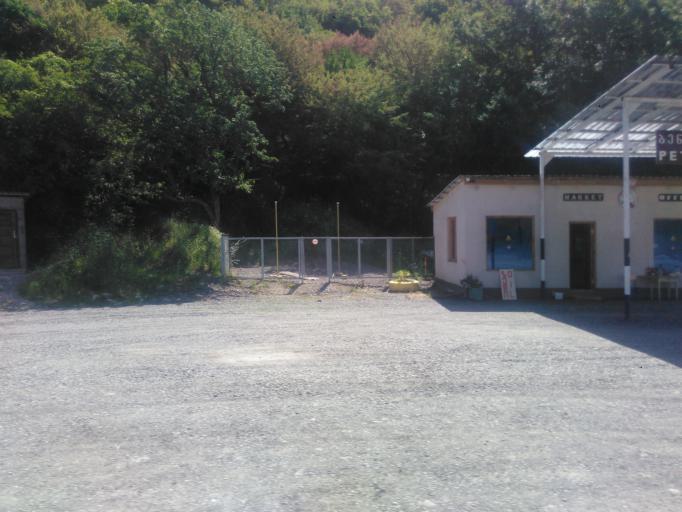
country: GE
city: Zhinvali
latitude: 42.2162
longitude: 44.8315
